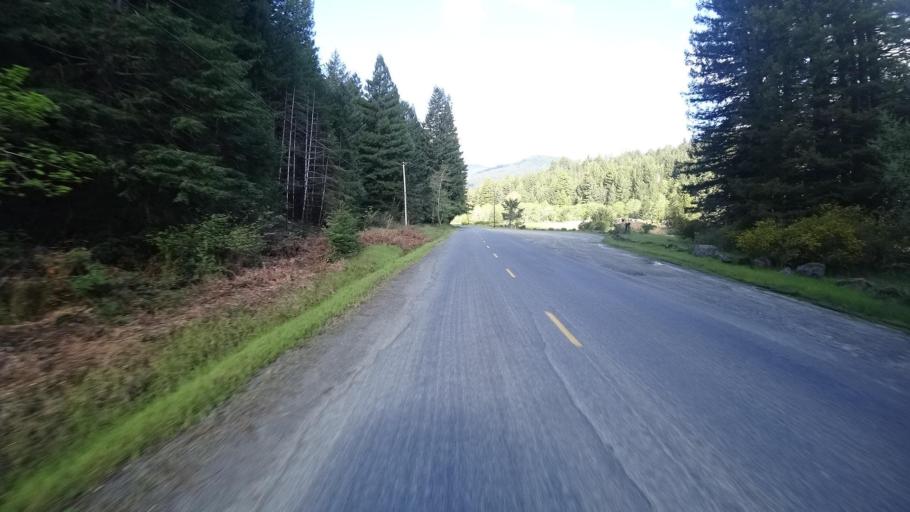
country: US
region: California
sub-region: Humboldt County
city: Rio Dell
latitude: 40.3503
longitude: -124.0147
